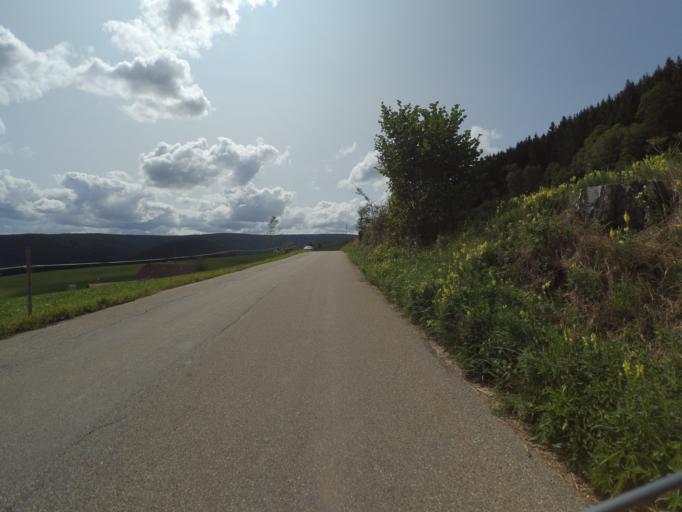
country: DE
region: Baden-Wuerttemberg
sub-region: Freiburg Region
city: Friedenweiler
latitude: 47.9169
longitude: 8.2333
